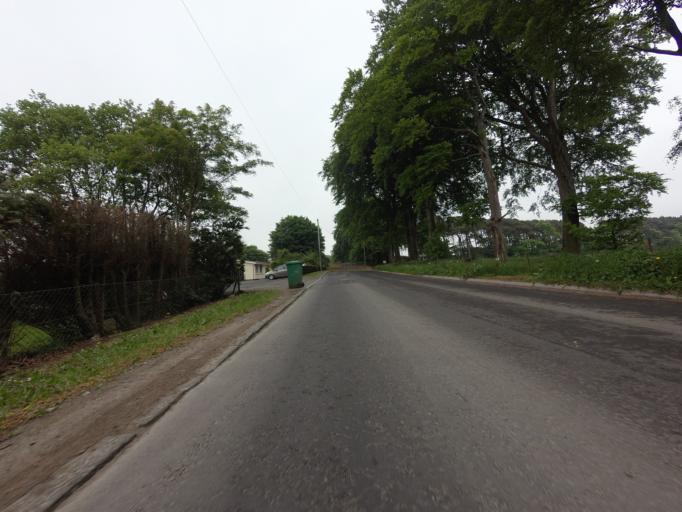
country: GB
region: Scotland
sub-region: Fife
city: Townhill
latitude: 56.0989
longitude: -3.4463
